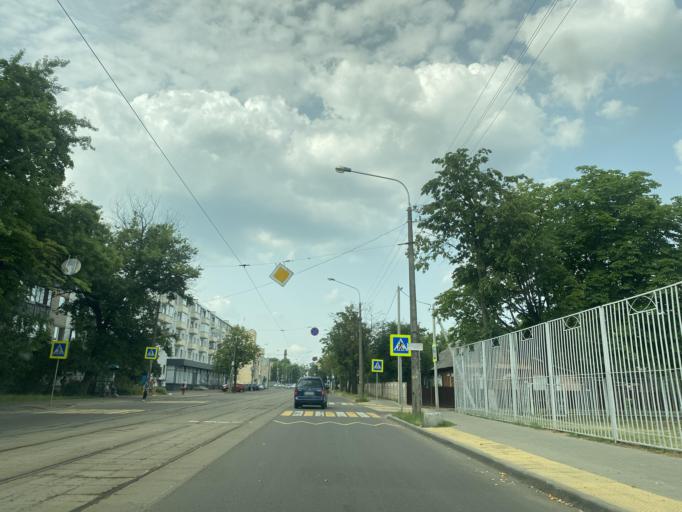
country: BY
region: Minsk
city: Minsk
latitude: 53.9300
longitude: 27.5437
